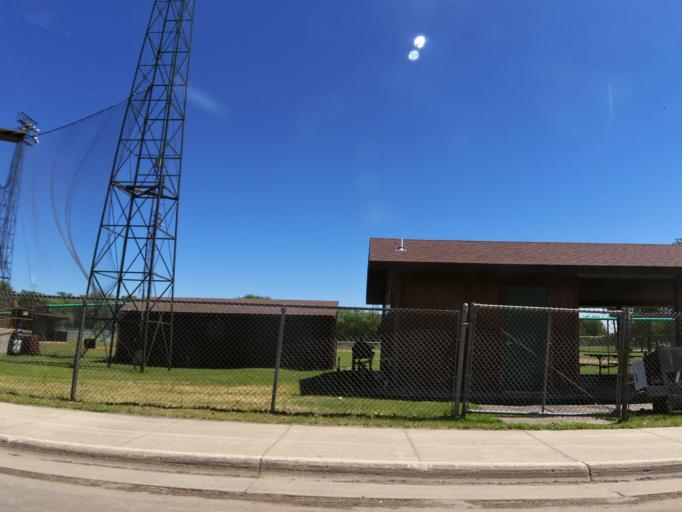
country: US
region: Minnesota
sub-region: Becker County
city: Detroit Lakes
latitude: 46.8085
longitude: -95.8458
